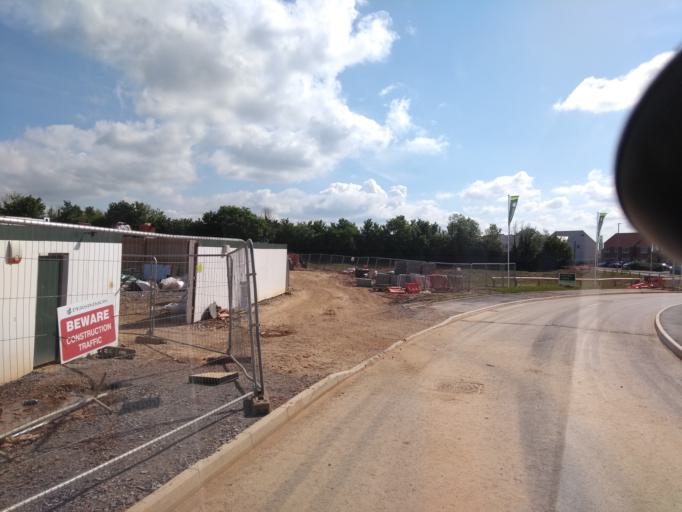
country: GB
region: England
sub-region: Somerset
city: Creech Saint Michael
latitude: 51.0397
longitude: -3.0598
